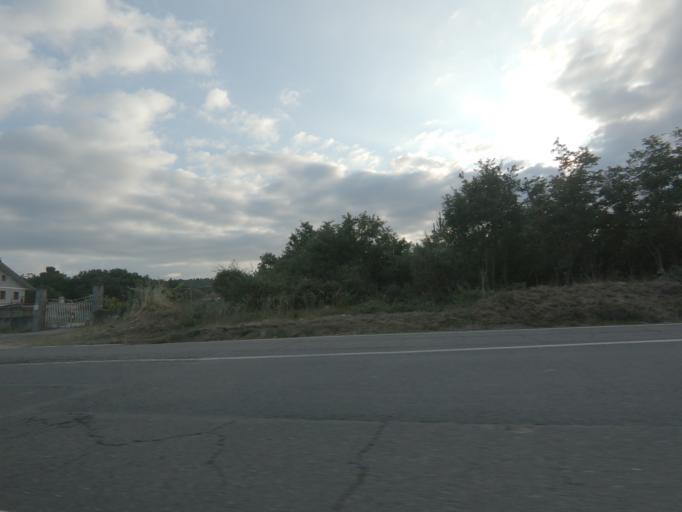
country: ES
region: Galicia
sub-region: Provincia de Ourense
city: Taboadela
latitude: 42.2676
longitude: -7.8367
